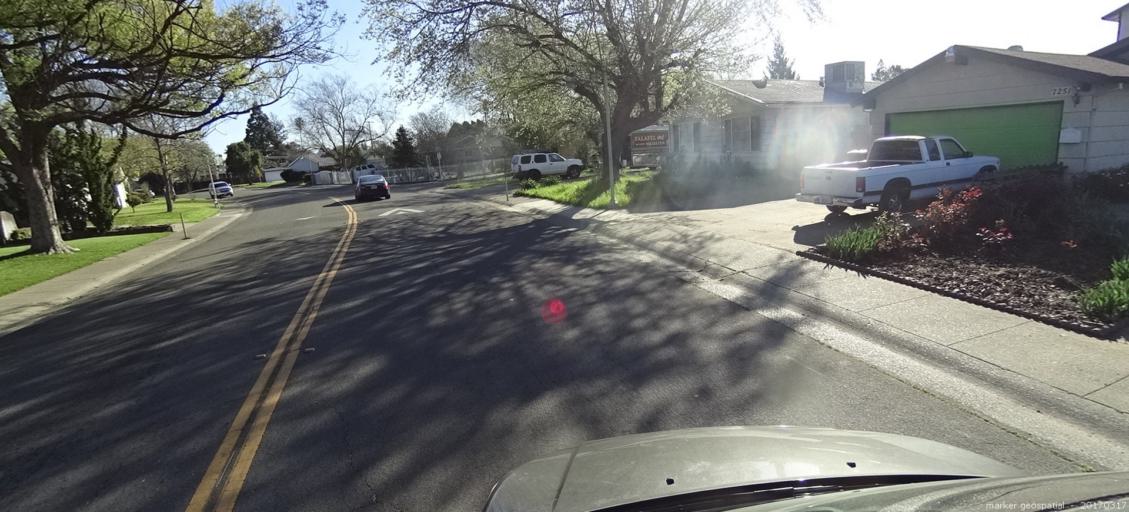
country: US
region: California
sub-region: Sacramento County
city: Parkway
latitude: 38.4936
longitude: -121.5046
